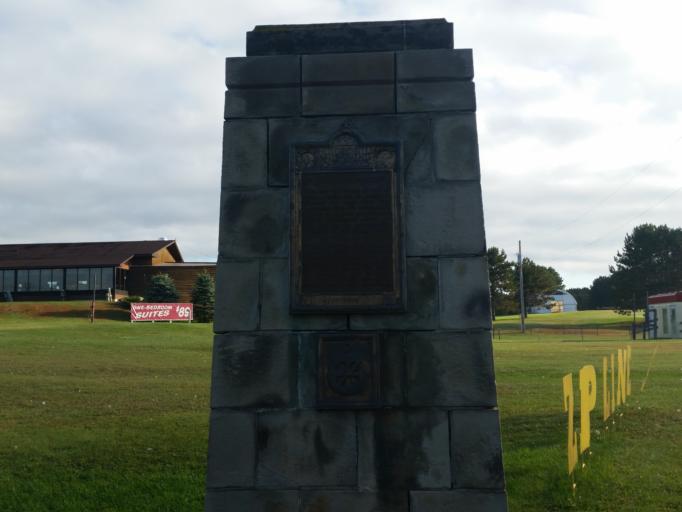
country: CA
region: Ontario
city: Renfrew
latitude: 45.5987
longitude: -76.8445
